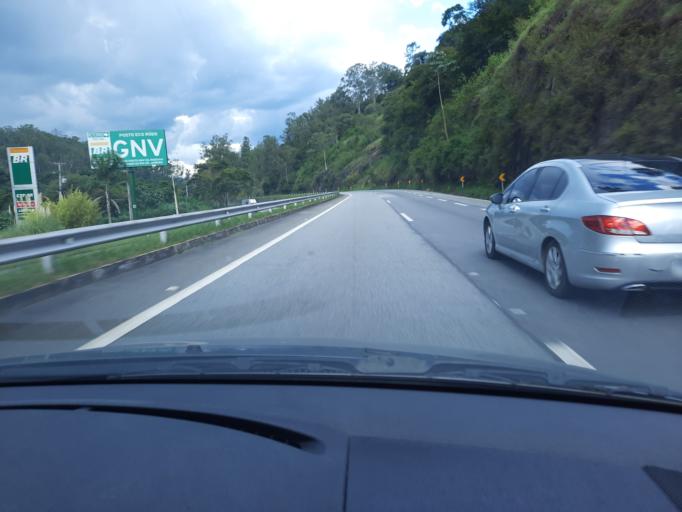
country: BR
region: Rio de Janeiro
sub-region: Petropolis
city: Petropolis
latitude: -22.4376
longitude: -43.1771
